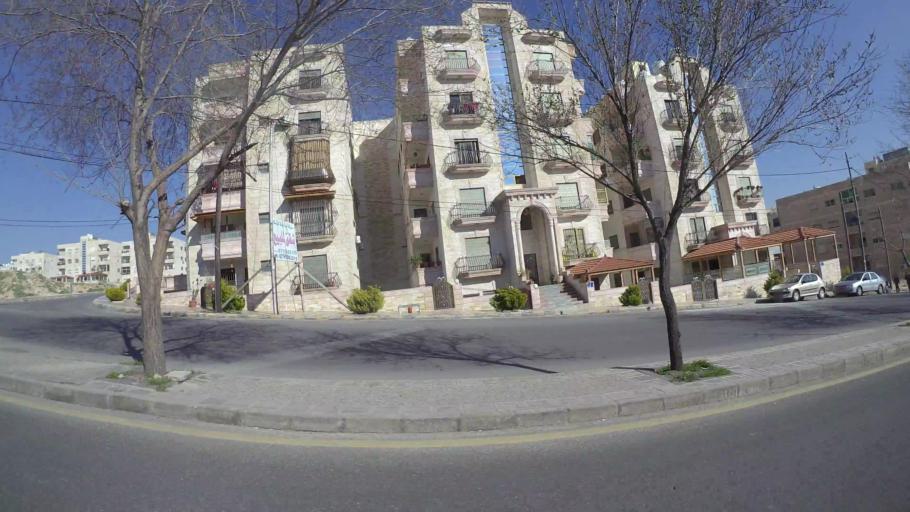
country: JO
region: Amman
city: Amman
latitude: 31.9773
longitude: 35.9388
